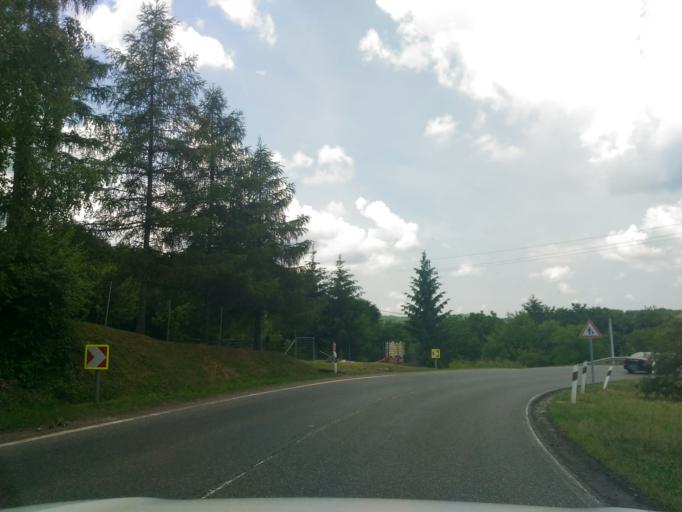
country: HU
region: Baranya
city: Komlo
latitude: 46.1574
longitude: 18.2386
